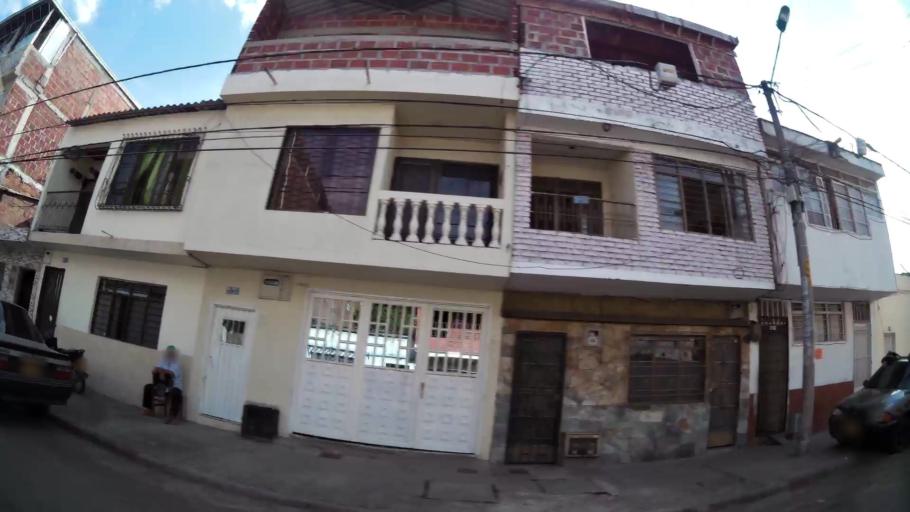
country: CO
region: Valle del Cauca
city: Cali
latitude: 3.4719
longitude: -76.5129
